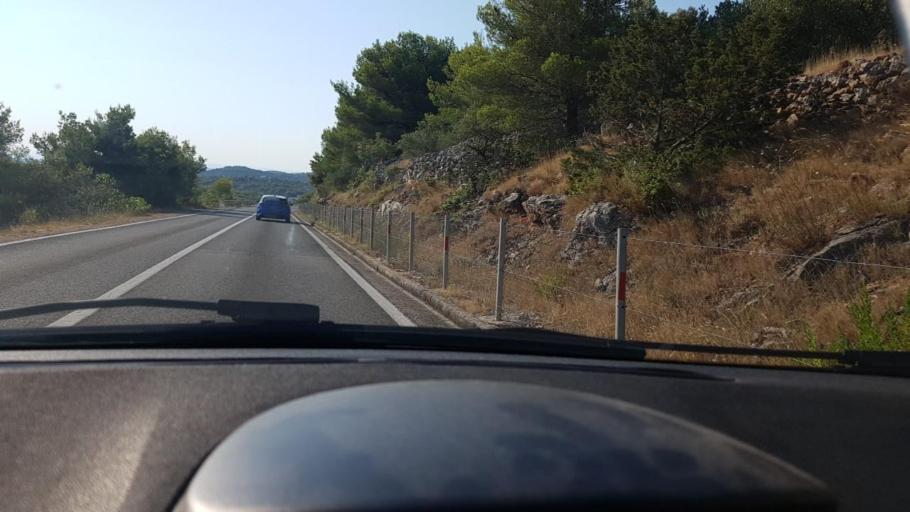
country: HR
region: Sibensko-Kniniska
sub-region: Grad Sibenik
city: Tisno
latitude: 43.7950
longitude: 15.6229
